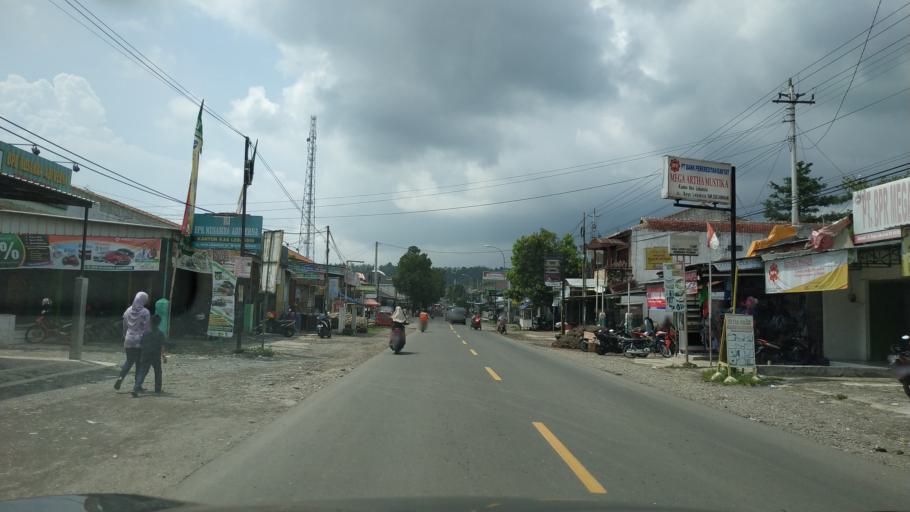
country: ID
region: Central Java
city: Lebaksiu
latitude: -7.0466
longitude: 109.1432
